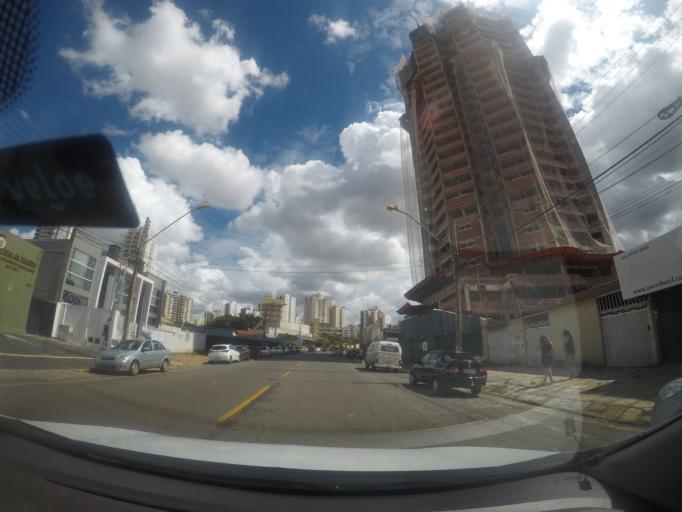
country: BR
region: Goias
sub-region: Goiania
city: Goiania
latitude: -16.6845
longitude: -49.2774
